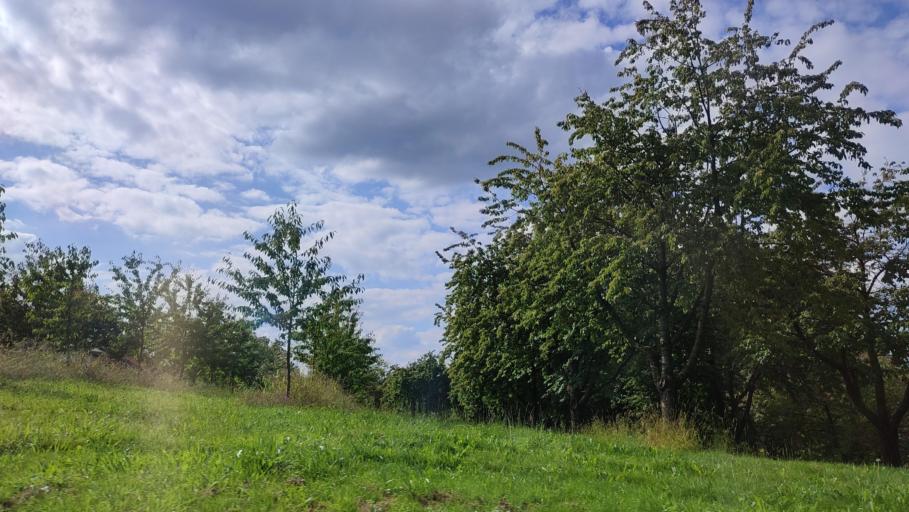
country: DE
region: Baden-Wuerttemberg
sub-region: Freiburg Region
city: Appenweier
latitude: 48.5227
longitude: 8.0062
